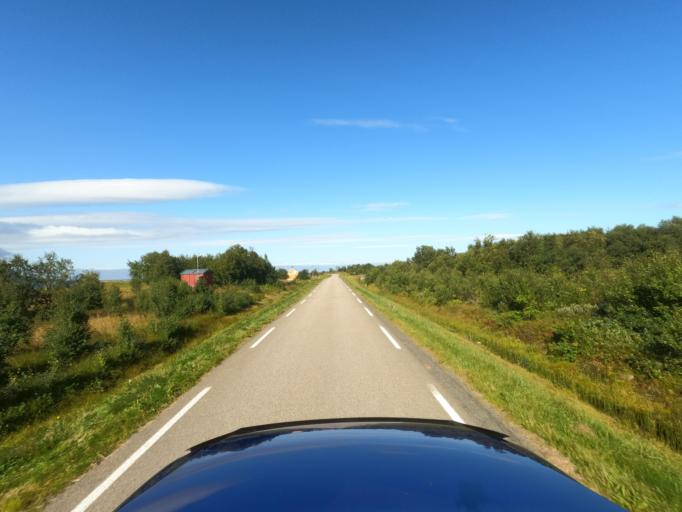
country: NO
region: Nordland
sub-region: Vestvagoy
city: Evjen
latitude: 68.3289
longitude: 14.0947
